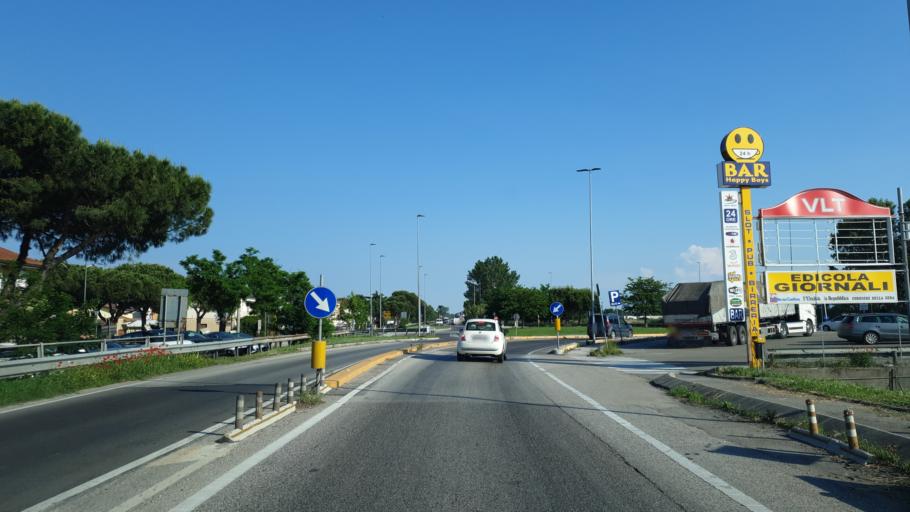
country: IT
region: Emilia-Romagna
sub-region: Provincia di Ravenna
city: Fosso Ghiaia
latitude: 44.3522
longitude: 12.2578
